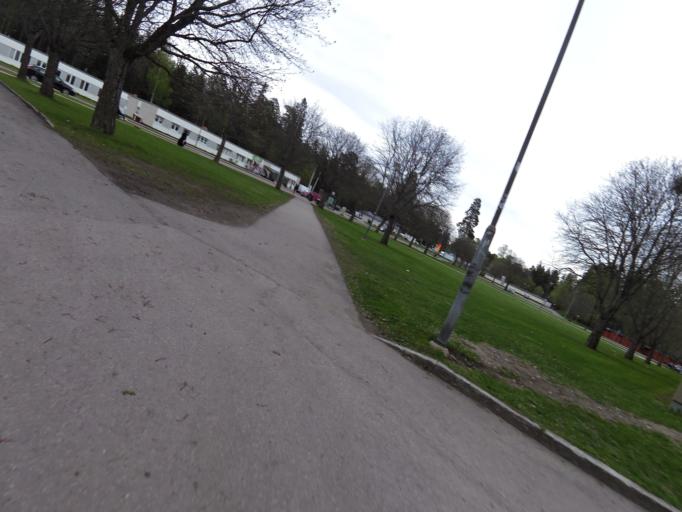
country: SE
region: Gaevleborg
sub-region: Gavle Kommun
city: Gavle
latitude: 60.6902
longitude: 17.1242
